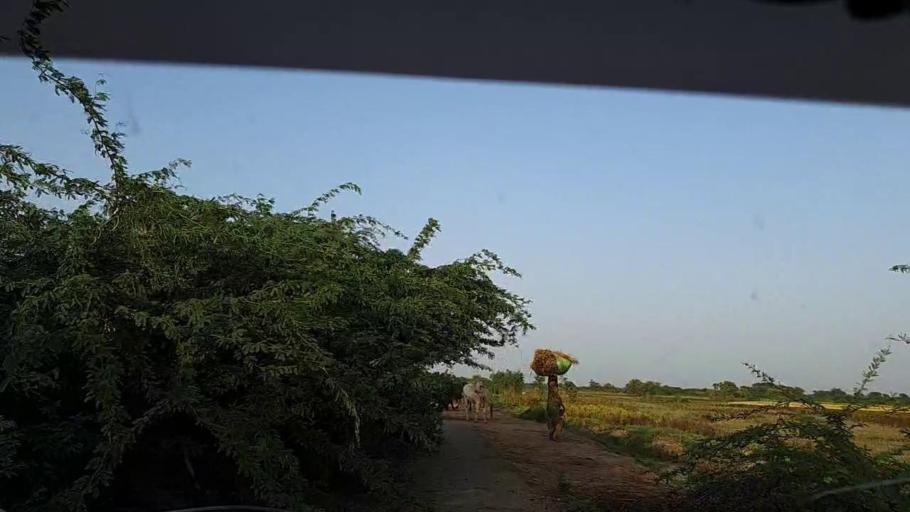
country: PK
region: Sindh
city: Kadhan
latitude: 24.5464
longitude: 68.9573
